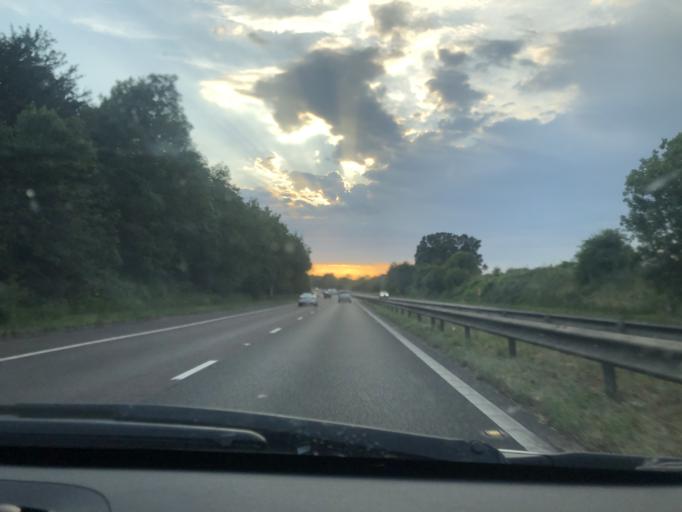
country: GB
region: England
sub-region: Kent
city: Newington
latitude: 51.3382
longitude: 0.6403
